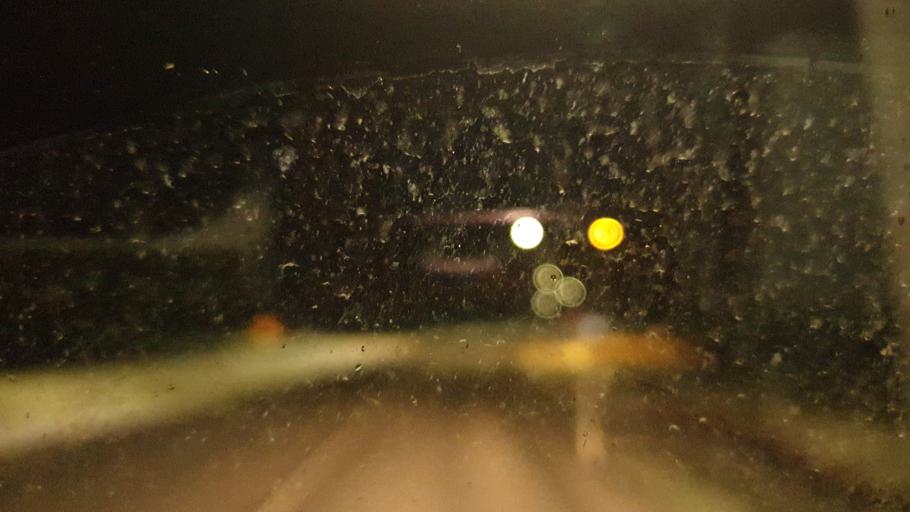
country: FI
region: Southern Savonia
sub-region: Pieksaemaeki
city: Juva
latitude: 61.8775
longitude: 27.7738
